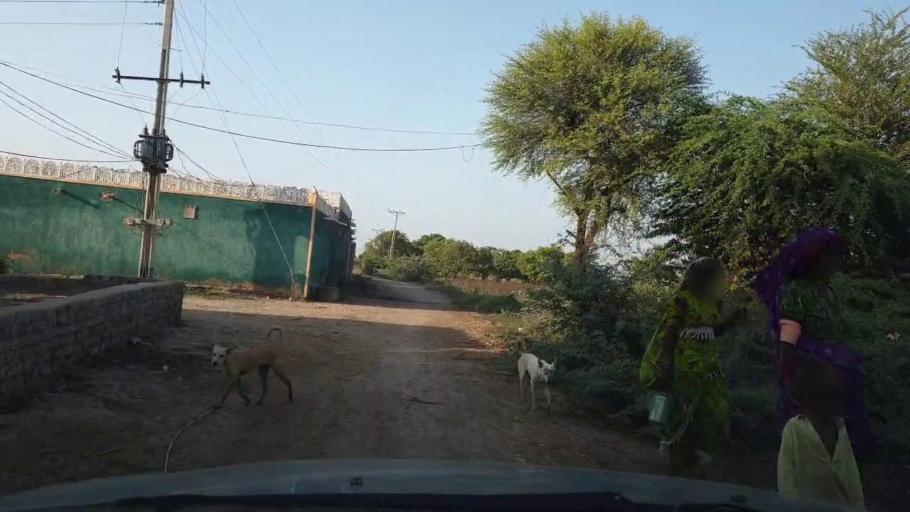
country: PK
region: Sindh
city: Tando Ghulam Ali
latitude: 25.1469
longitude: 68.9487
